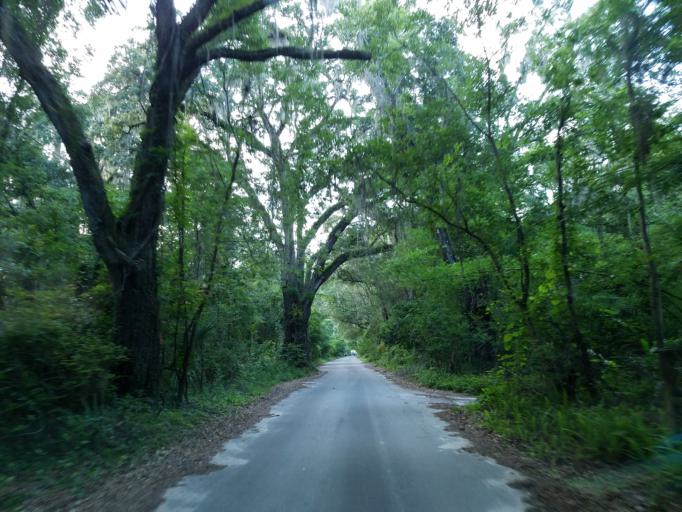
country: US
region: Florida
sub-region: Alachua County
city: Gainesville
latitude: 29.4996
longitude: -82.2827
